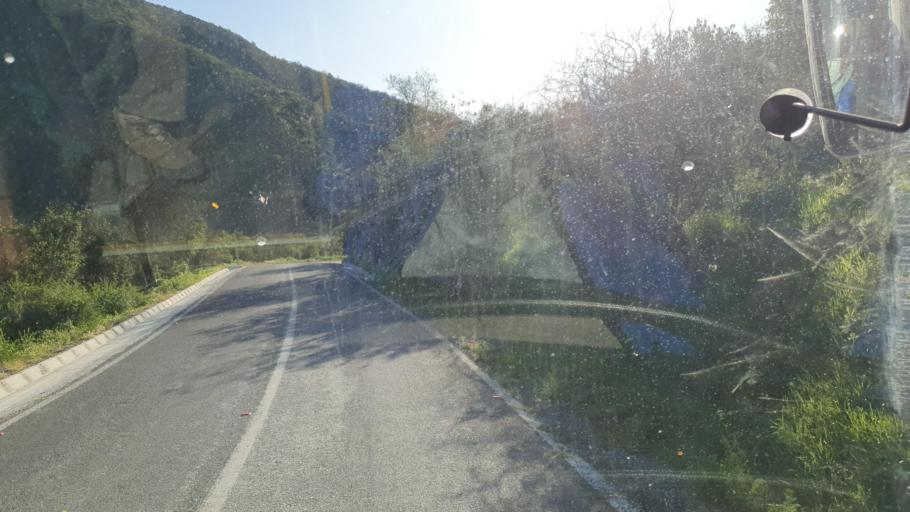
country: CL
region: Valparaiso
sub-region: Provincia de Marga Marga
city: Limache
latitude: -33.1974
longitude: -71.2702
